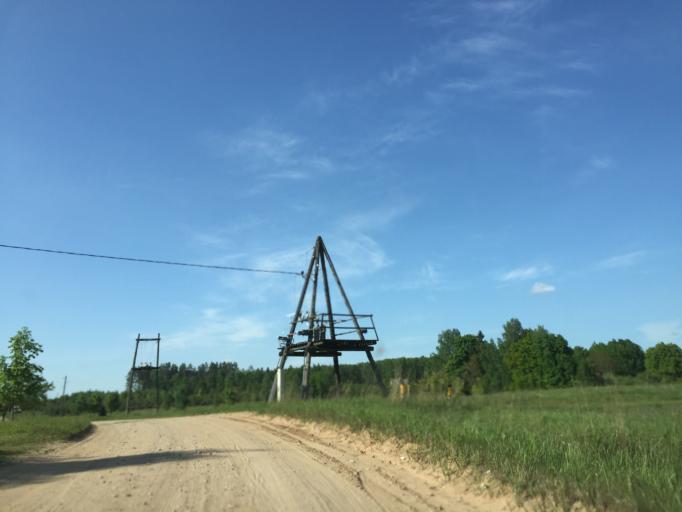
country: LV
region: Salaspils
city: Salaspils
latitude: 56.8066
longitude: 24.3725
